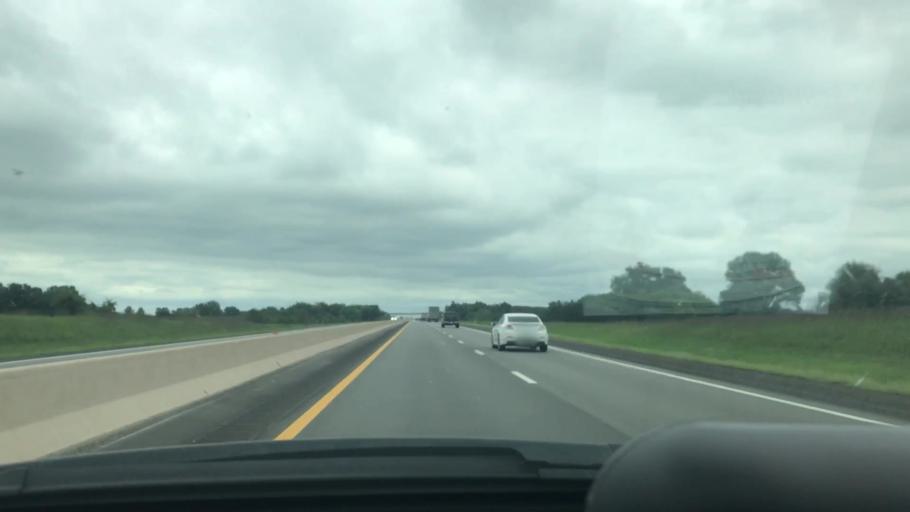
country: US
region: Oklahoma
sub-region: Craig County
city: Vinita
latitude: 36.6663
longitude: -95.0780
